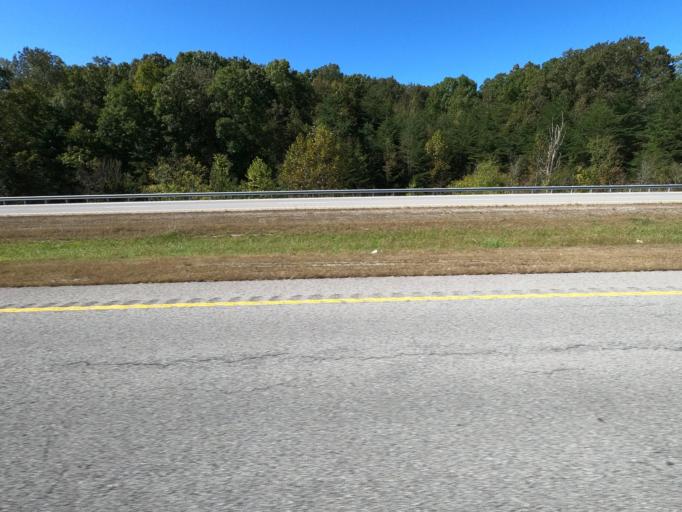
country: US
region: Tennessee
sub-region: Maury County
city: Mount Pleasant
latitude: 35.4634
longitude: -87.2671
